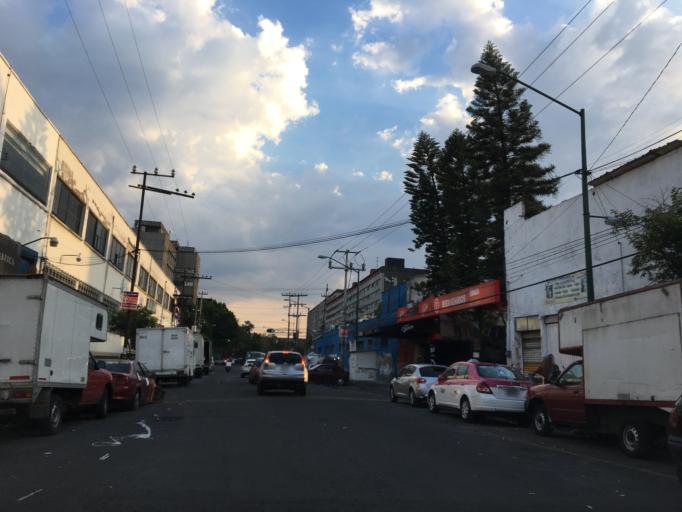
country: MX
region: Mexico City
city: Cuauhtemoc
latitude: 19.4562
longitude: -99.1401
